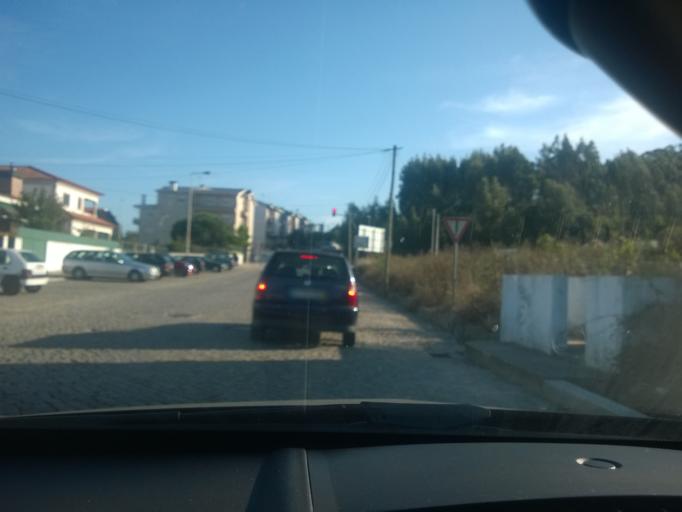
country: PT
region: Porto
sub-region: Maia
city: Anta
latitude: 41.2685
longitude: -8.6189
